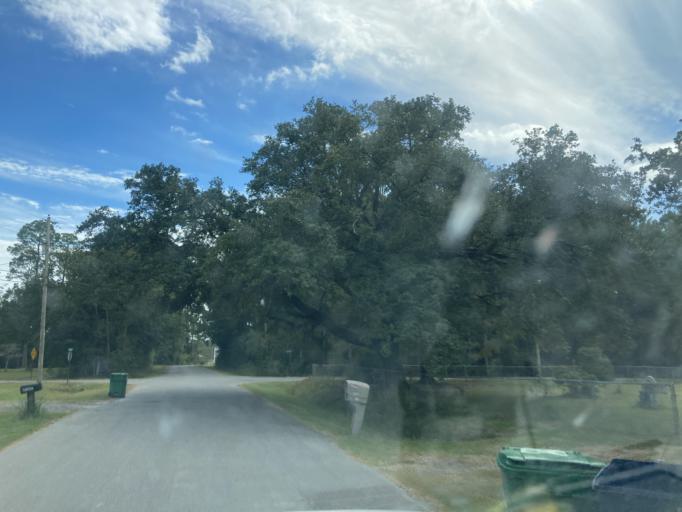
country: US
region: Mississippi
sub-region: Jackson County
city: Saint Martin
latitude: 30.4380
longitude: -88.8738
